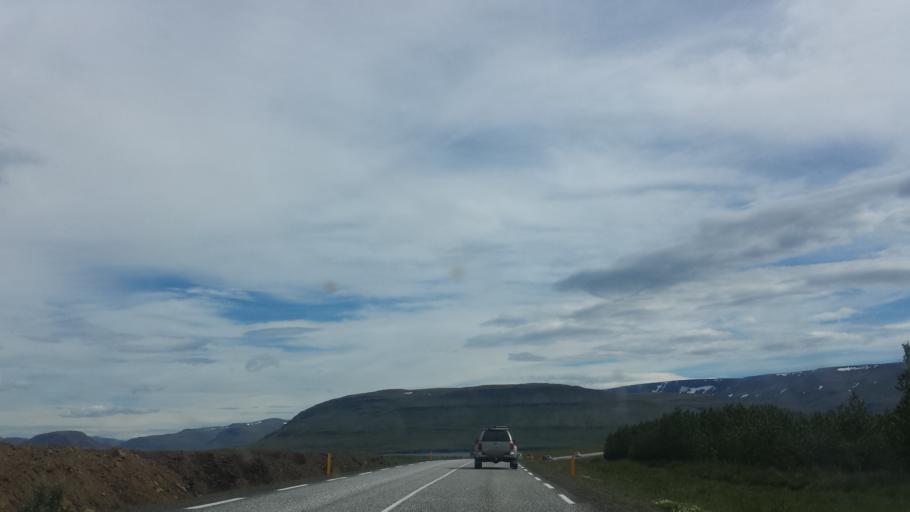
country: IS
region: West
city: Borgarnes
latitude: 64.3609
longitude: -21.8121
